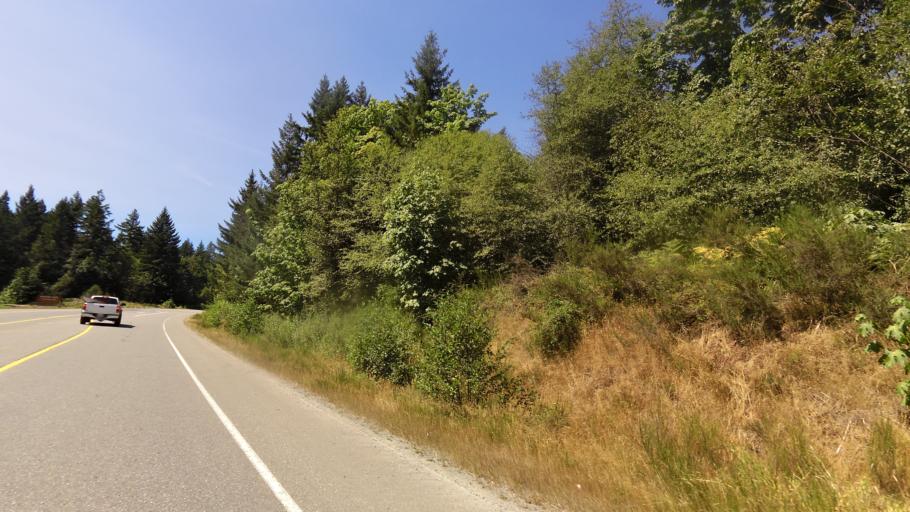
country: CA
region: British Columbia
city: Port Alberni
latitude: 49.2955
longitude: -124.9314
